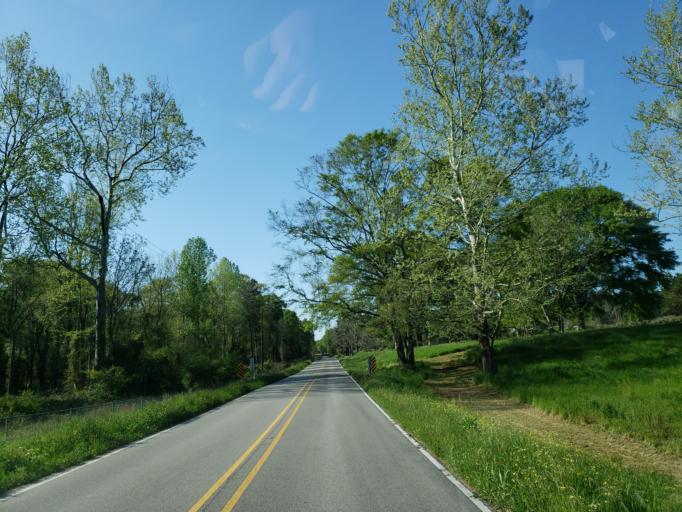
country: US
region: Mississippi
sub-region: Jones County
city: Ellisville
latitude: 31.5764
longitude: -89.3727
